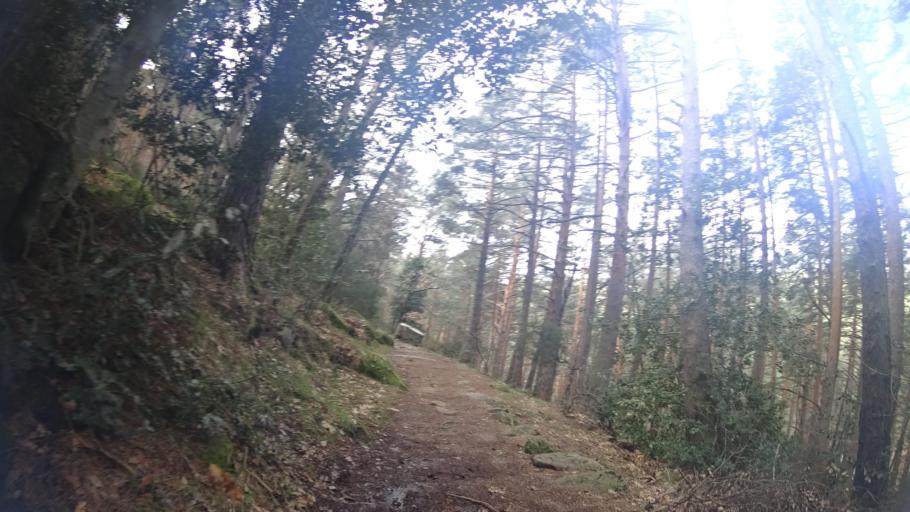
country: ES
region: Madrid
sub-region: Provincia de Madrid
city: Canencia
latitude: 40.8715
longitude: -3.7805
